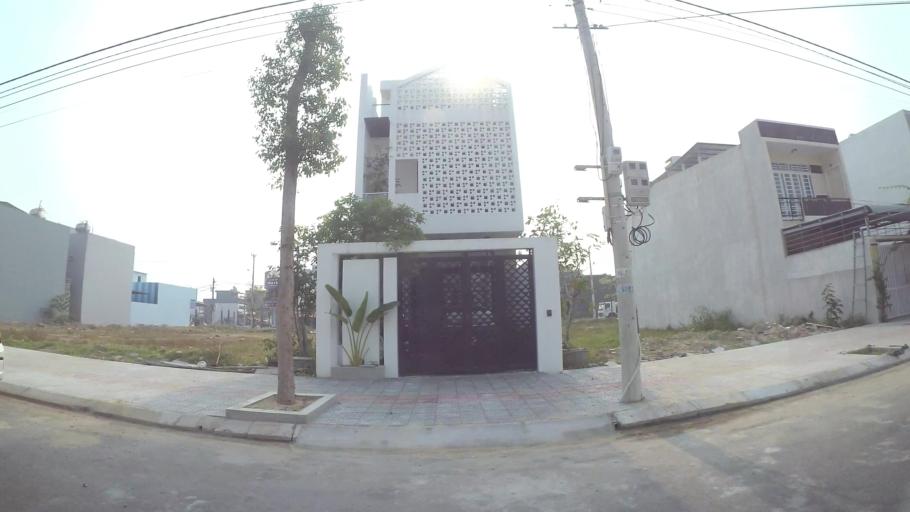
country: VN
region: Da Nang
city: Ngu Hanh Son
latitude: 16.0110
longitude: 108.2289
